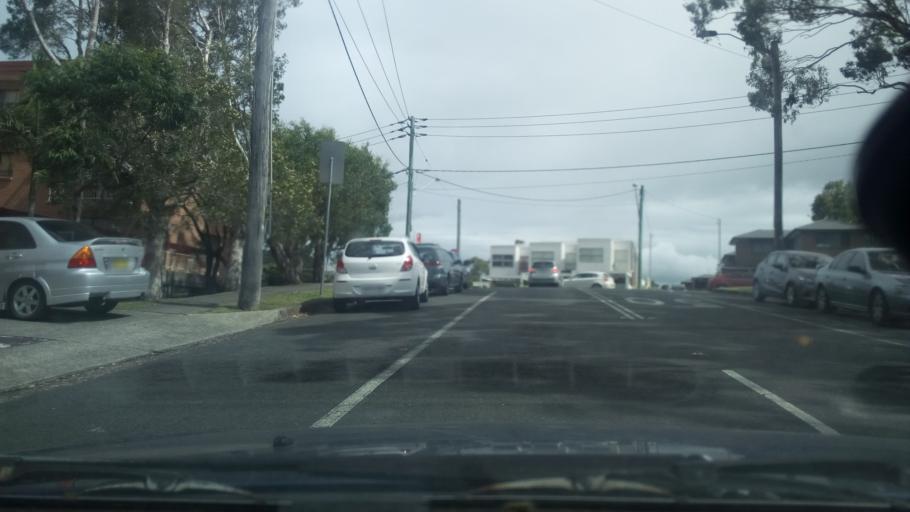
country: AU
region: New South Wales
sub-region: Wollongong
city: West Wollongong
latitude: -34.4251
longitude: 150.8745
